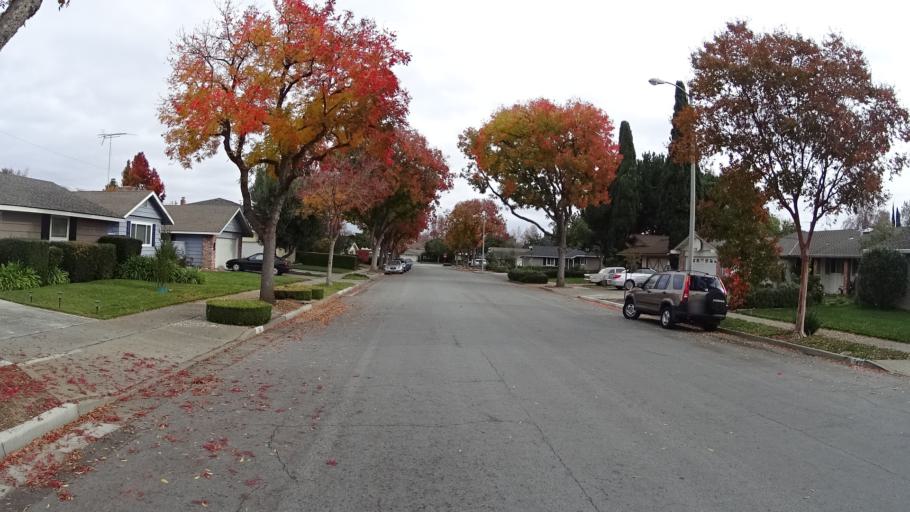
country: US
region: California
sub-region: Santa Clara County
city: Sunnyvale
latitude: 37.3615
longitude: -122.0433
